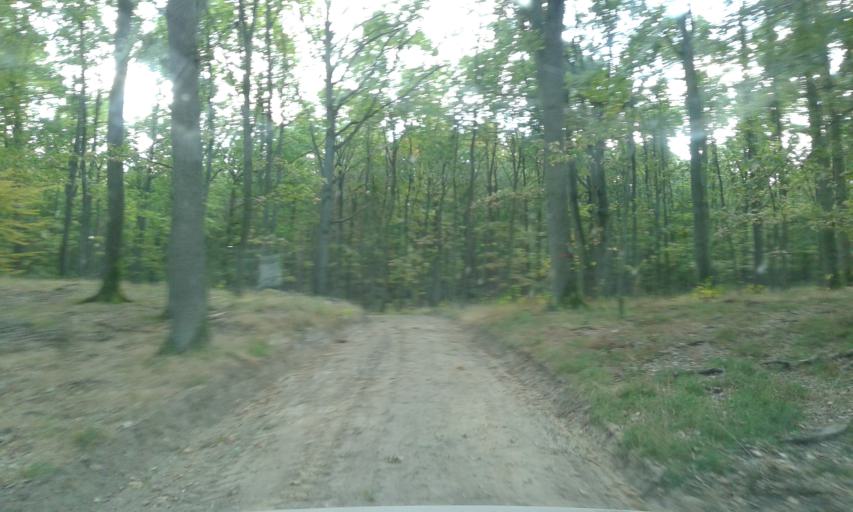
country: PL
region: West Pomeranian Voivodeship
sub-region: Powiat stargardzki
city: Dolice
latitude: 53.2311
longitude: 15.2454
